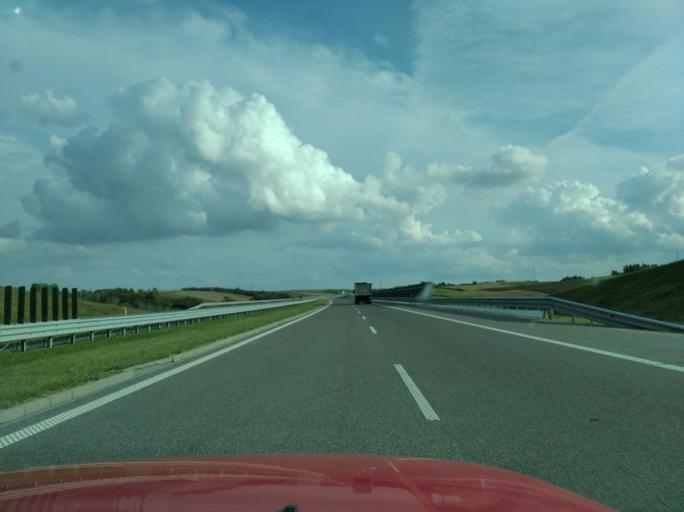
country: PL
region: Subcarpathian Voivodeship
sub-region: Powiat jaroslawski
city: Wierzbna
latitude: 50.0216
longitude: 22.5820
